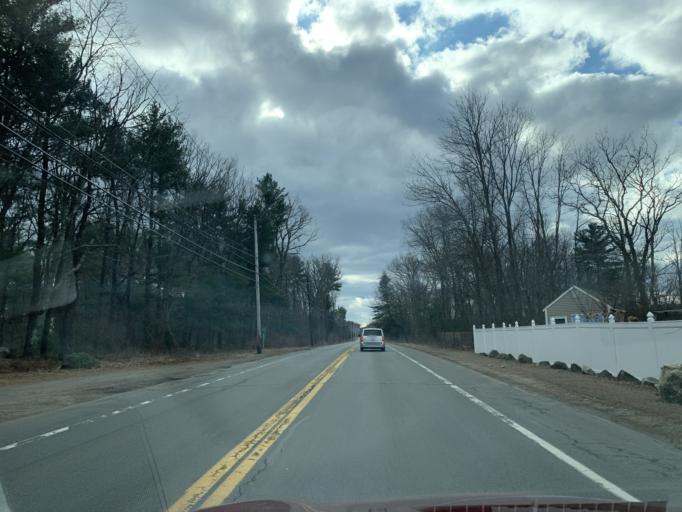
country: US
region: Massachusetts
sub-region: Essex County
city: Newburyport
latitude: 42.7752
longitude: -70.8849
